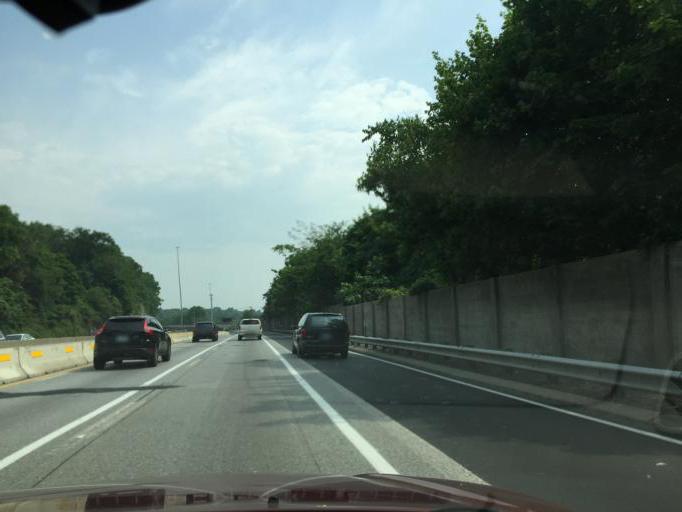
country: US
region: New York
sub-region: Westchester County
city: Mamaroneck
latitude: 40.9542
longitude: -73.7435
